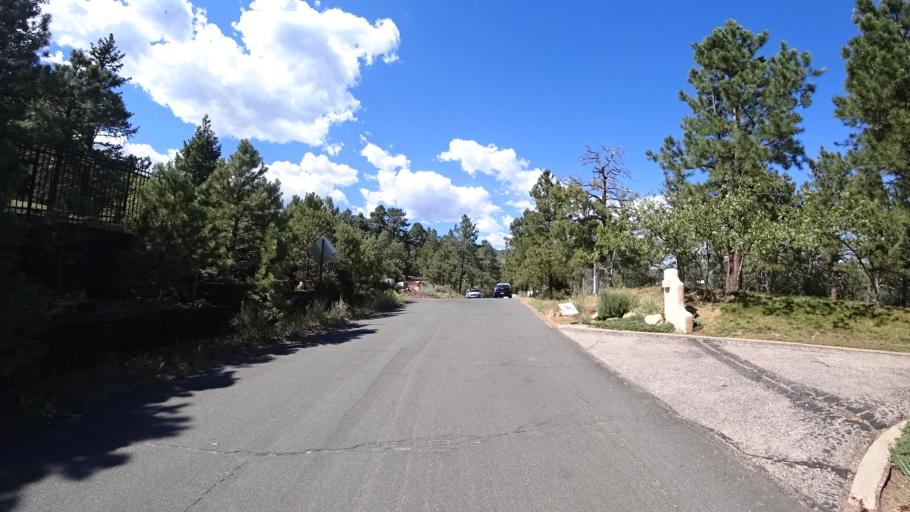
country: US
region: Colorado
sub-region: El Paso County
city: Colorado Springs
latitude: 38.7805
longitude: -104.8592
